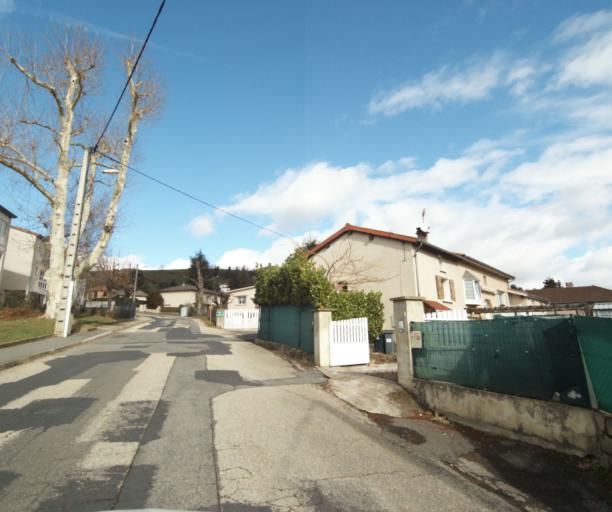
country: FR
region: Rhone-Alpes
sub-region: Departement de la Loire
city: La Talaudiere
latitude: 45.4868
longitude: 4.4292
